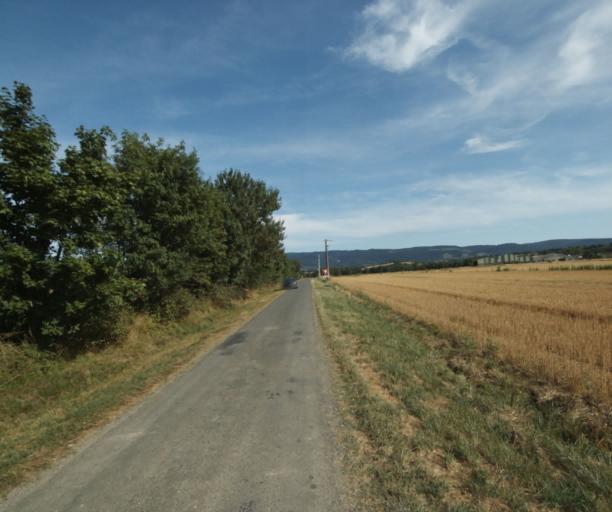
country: FR
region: Midi-Pyrenees
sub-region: Departement du Tarn
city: Soreze
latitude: 43.5088
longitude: 2.0566
